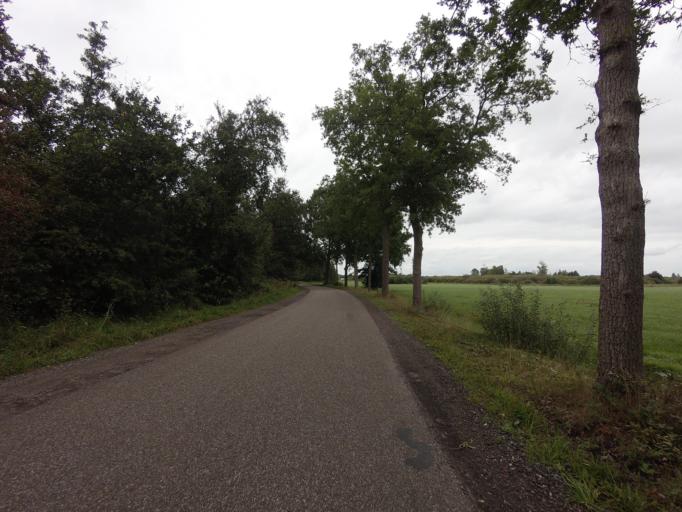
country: NL
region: Friesland
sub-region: Gemeente Weststellingwerf
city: Steggerda
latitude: 52.8749
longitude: 6.0931
